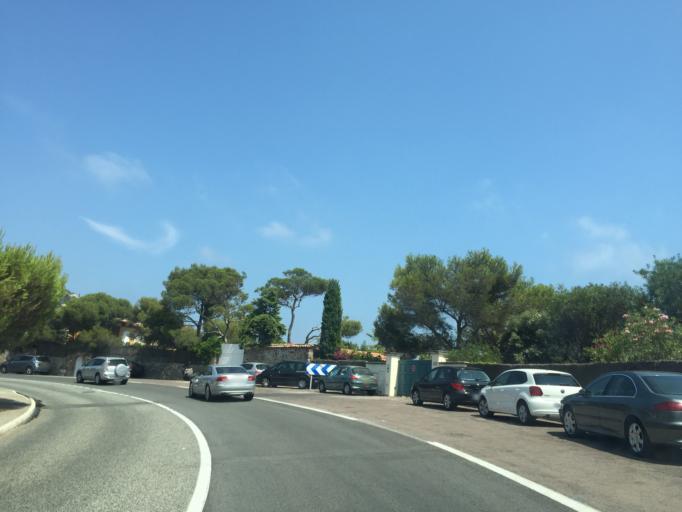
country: FR
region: Provence-Alpes-Cote d'Azur
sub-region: Departement des Alpes-Maritimes
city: Theoule-sur-Mer
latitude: 43.4269
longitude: 6.8776
